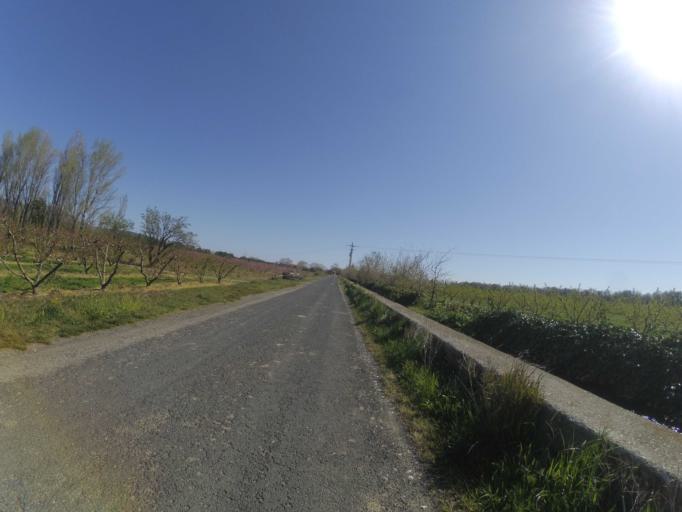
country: FR
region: Languedoc-Roussillon
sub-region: Departement des Pyrenees-Orientales
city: Millas
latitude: 42.6779
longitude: 2.6729
